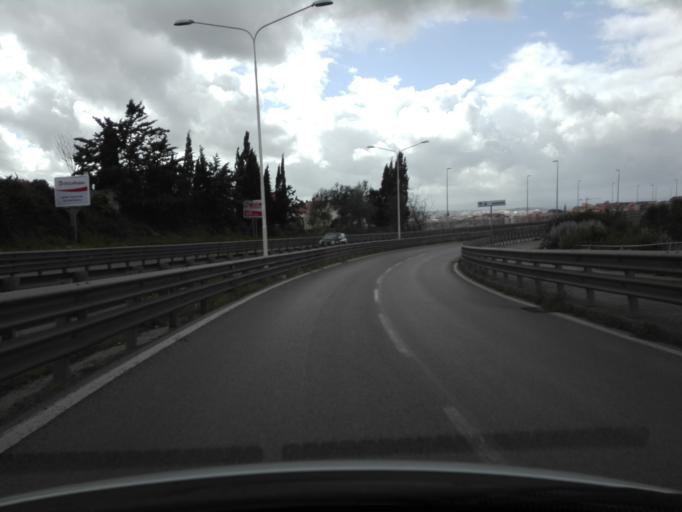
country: IT
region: Sardinia
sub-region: Provincia di Sassari
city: Sassari
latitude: 40.7310
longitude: 8.5732
